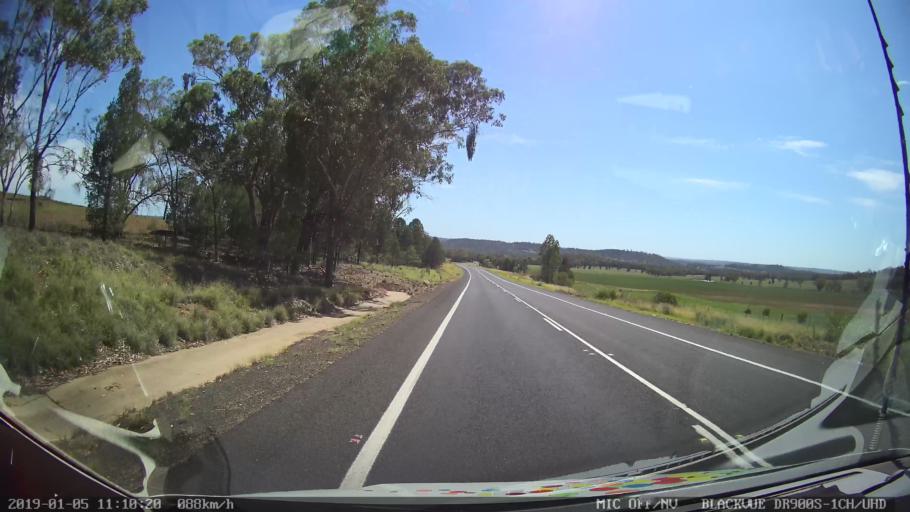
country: AU
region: New South Wales
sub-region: Warrumbungle Shire
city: Coonabarabran
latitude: -31.4076
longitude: 149.2433
